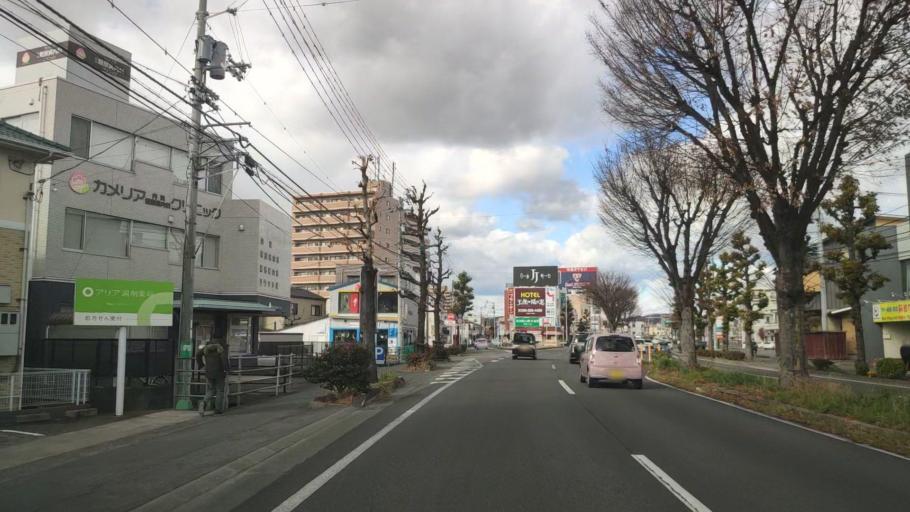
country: JP
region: Ehime
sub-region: Shikoku-chuo Shi
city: Matsuyama
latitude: 33.8152
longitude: 132.7773
